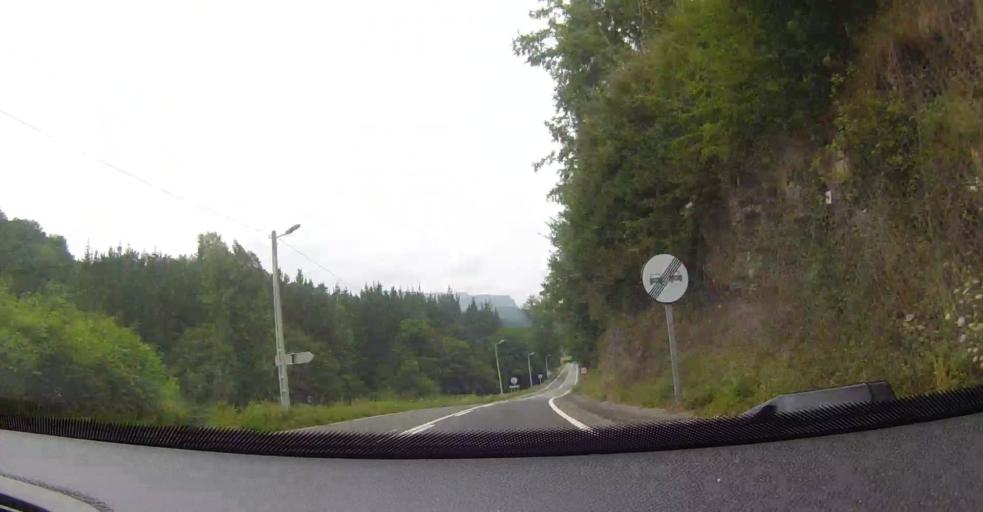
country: ES
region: Basque Country
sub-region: Bizkaia
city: Lanestosa
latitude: 43.2337
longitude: -3.3497
